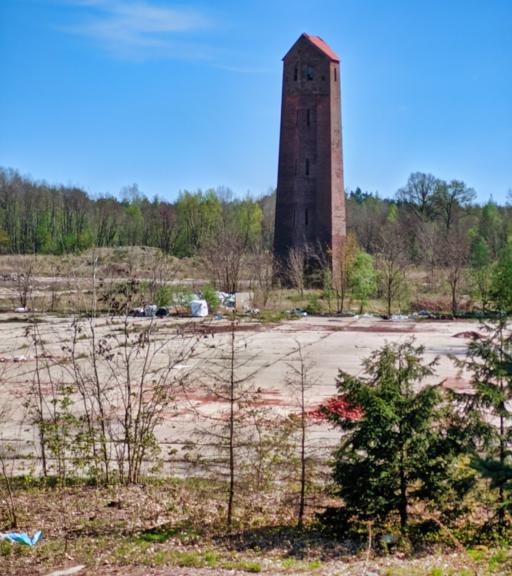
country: PL
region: Lubusz
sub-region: Powiat zarski
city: Kunice Zarskie
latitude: 51.5676
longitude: 15.1822
